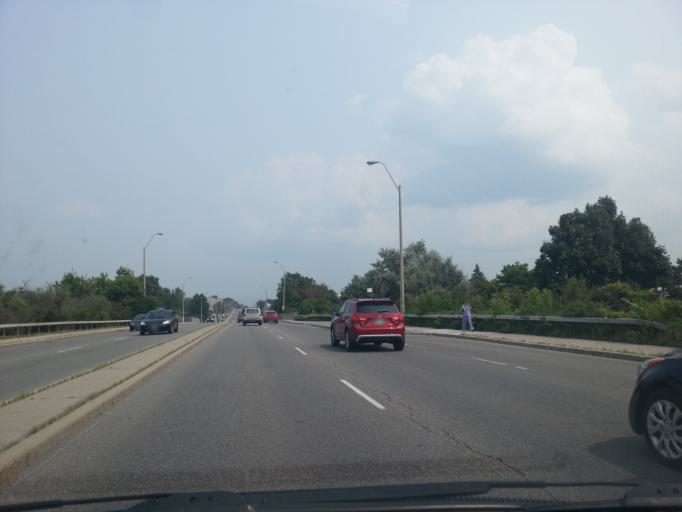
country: CA
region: Ontario
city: Ottawa
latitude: 45.4468
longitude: -75.6203
